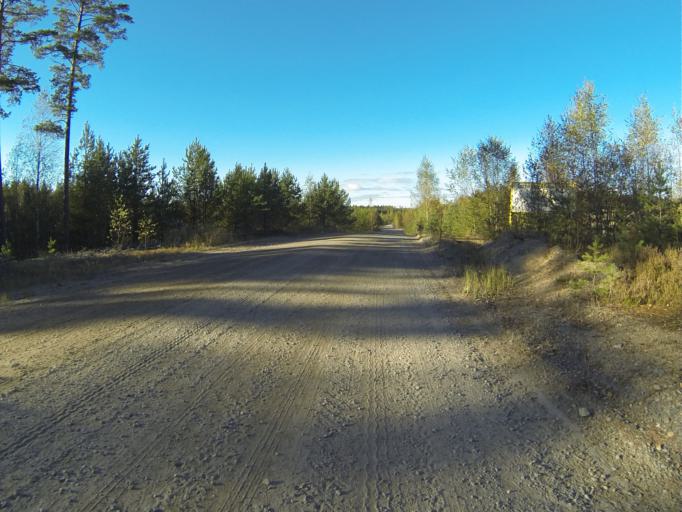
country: FI
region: Varsinais-Suomi
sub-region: Salo
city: Saerkisalo
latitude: 60.2210
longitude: 22.9896
